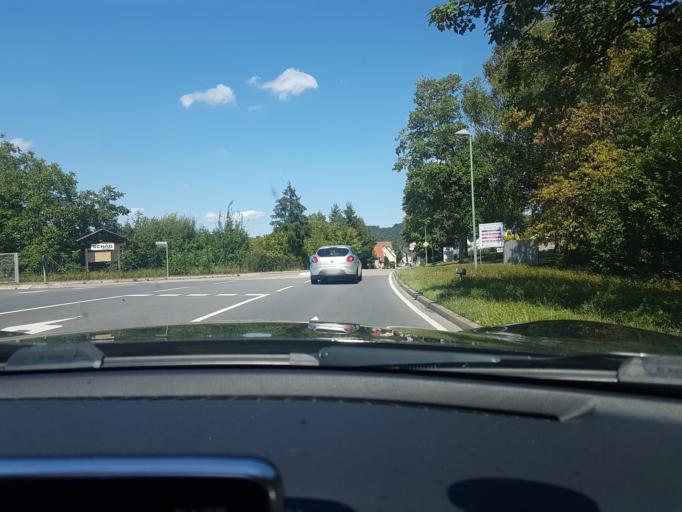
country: DE
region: Baden-Wuerttemberg
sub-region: Karlsruhe Region
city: Hassmersheim
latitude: 49.2894
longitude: 9.1450
